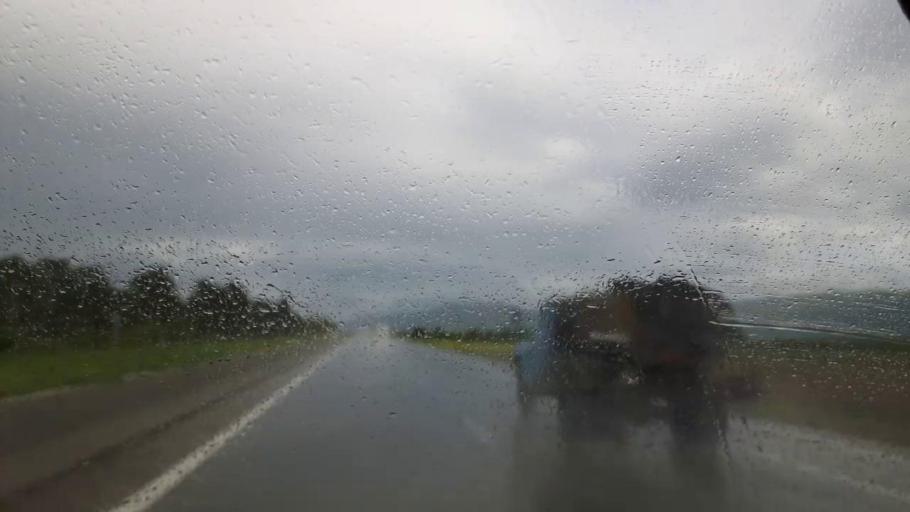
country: GE
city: Agara
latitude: 42.0408
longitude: 43.9297
